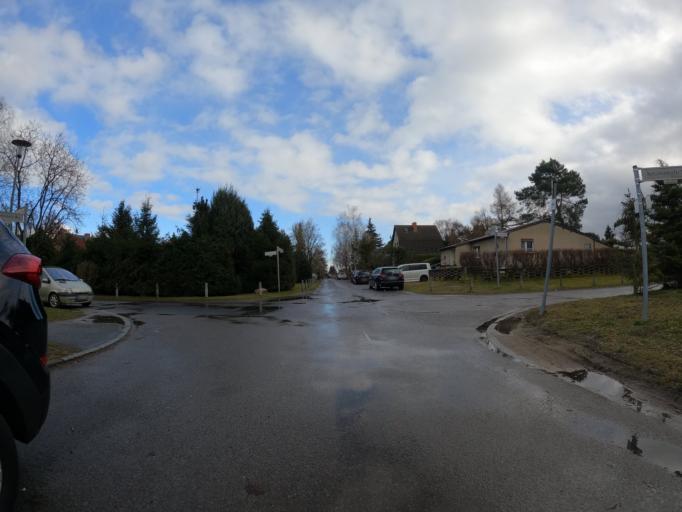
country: DE
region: Berlin
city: Marzahn
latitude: 52.5305
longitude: 13.5616
